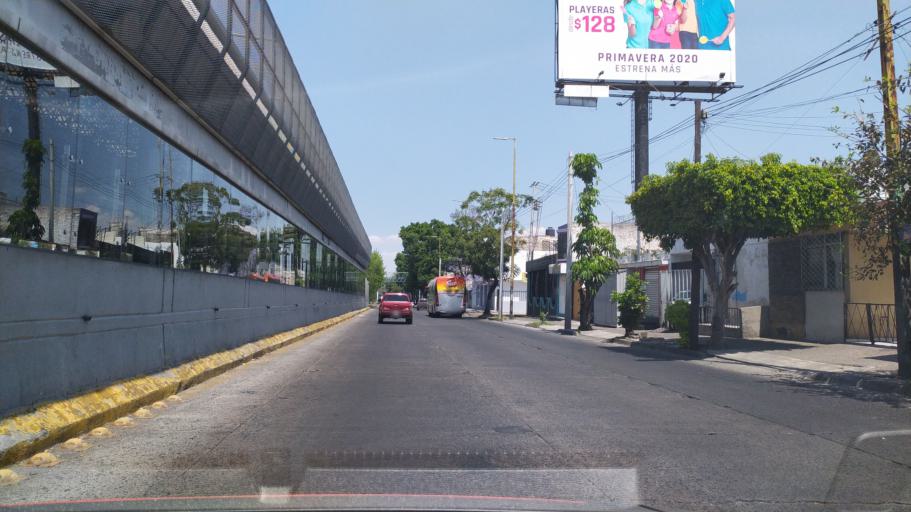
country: MX
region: Jalisco
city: Guadalajara
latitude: 20.6429
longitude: -103.3727
